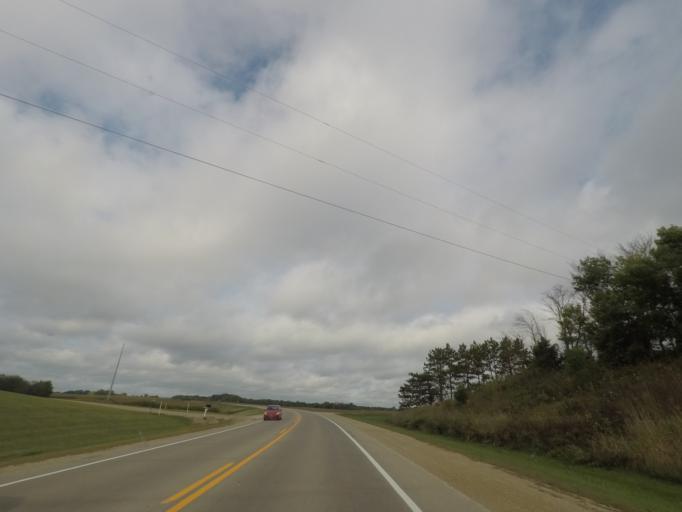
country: US
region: Wisconsin
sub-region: Jefferson County
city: Cambridge
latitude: 43.0182
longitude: -89.0375
